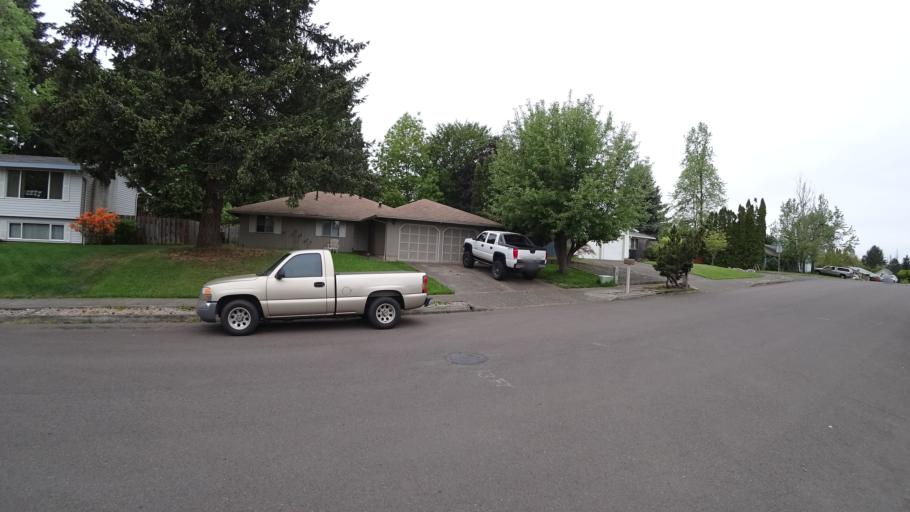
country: US
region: Oregon
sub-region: Washington County
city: Aloha
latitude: 45.5016
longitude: -122.8772
